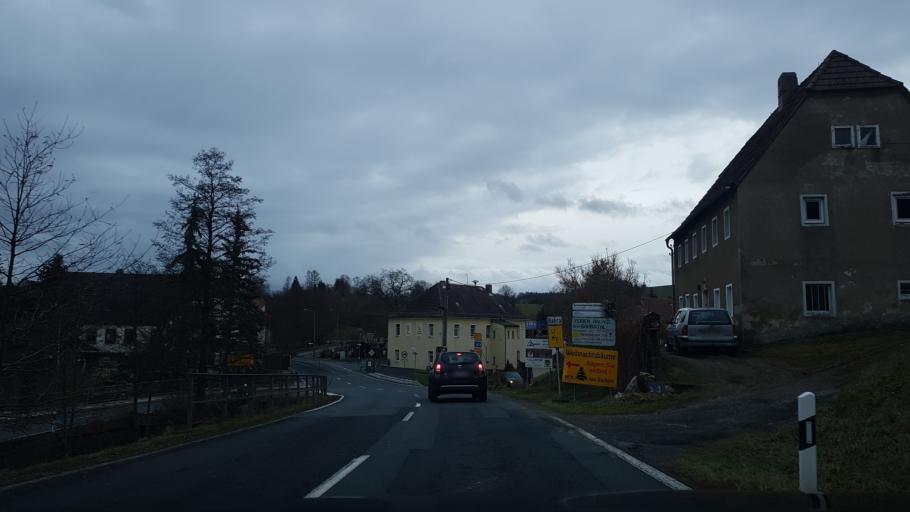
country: DE
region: Saxony
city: Dohma
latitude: 50.8295
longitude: 13.9732
